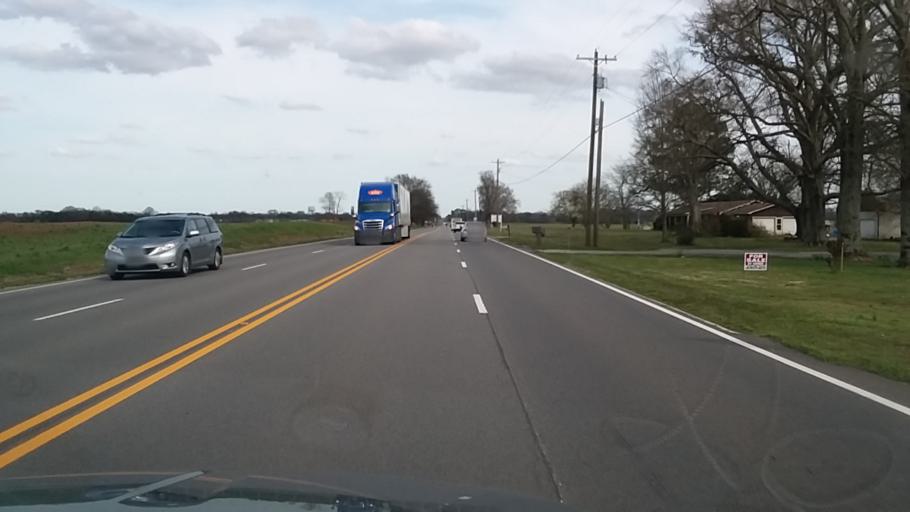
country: US
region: Alabama
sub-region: Lawrence County
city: Town Creek
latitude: 34.6819
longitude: -87.4366
